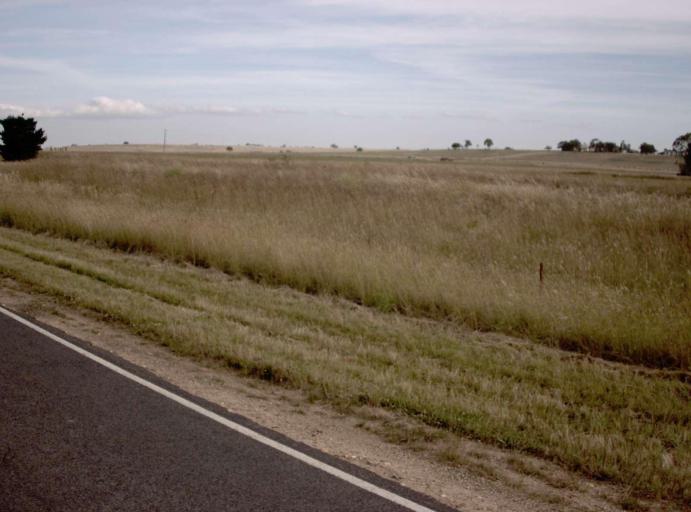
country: AU
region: Victoria
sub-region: Wellington
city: Heyfield
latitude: -38.0189
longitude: 146.7249
